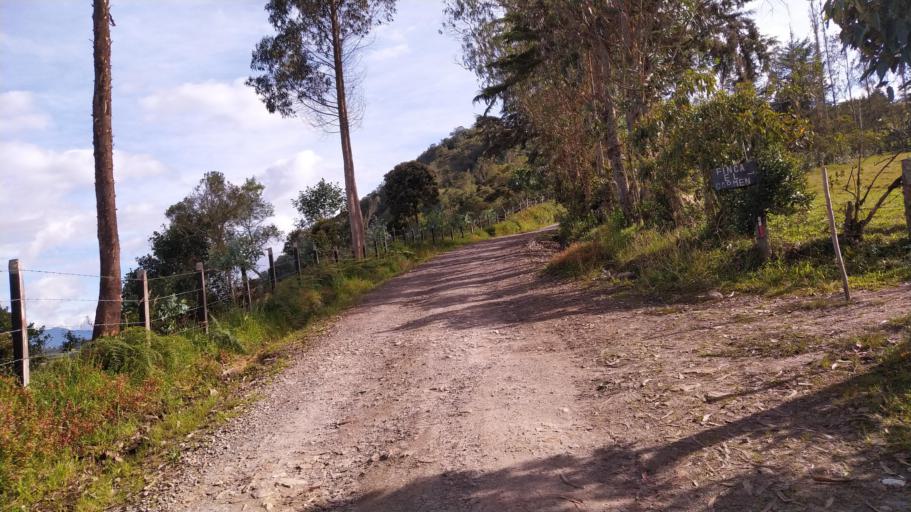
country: CO
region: Cundinamarca
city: Tenza
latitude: 5.0882
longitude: -73.4789
